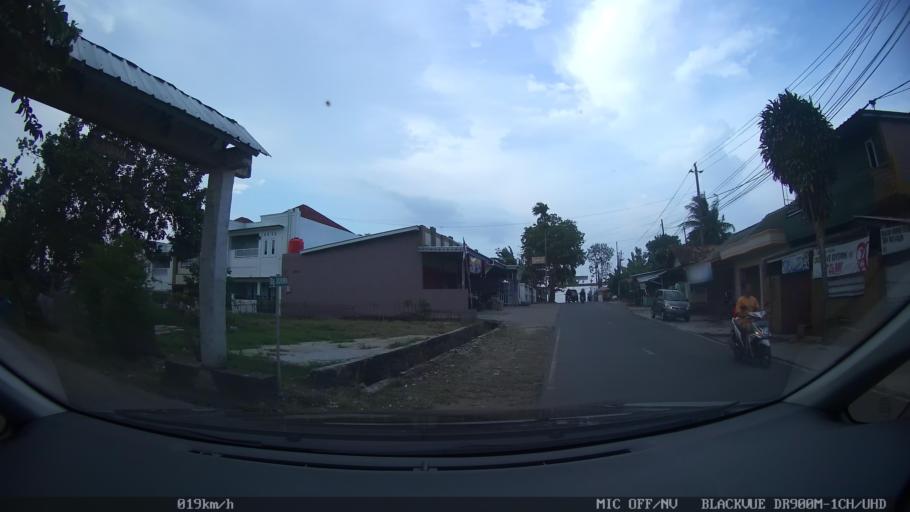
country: ID
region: Lampung
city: Kedaton
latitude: -5.4028
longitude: 105.2332
